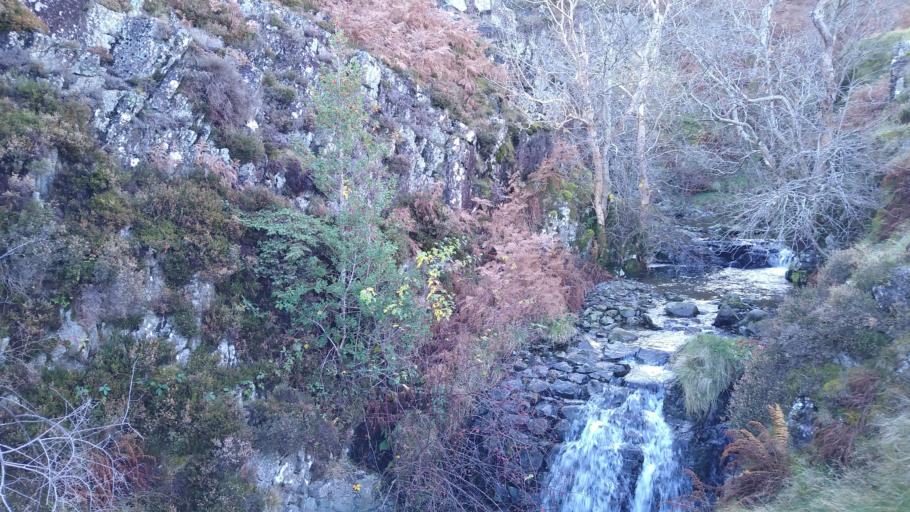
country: GB
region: England
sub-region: Cumbria
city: Keswick
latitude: 54.5549
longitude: -3.0518
